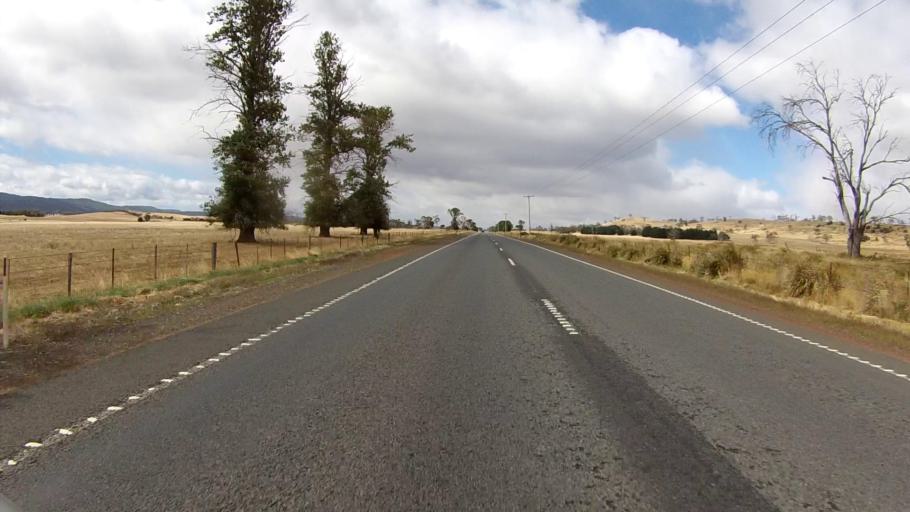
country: AU
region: Tasmania
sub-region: Northern Midlands
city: Evandale
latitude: -41.9579
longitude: 147.4973
